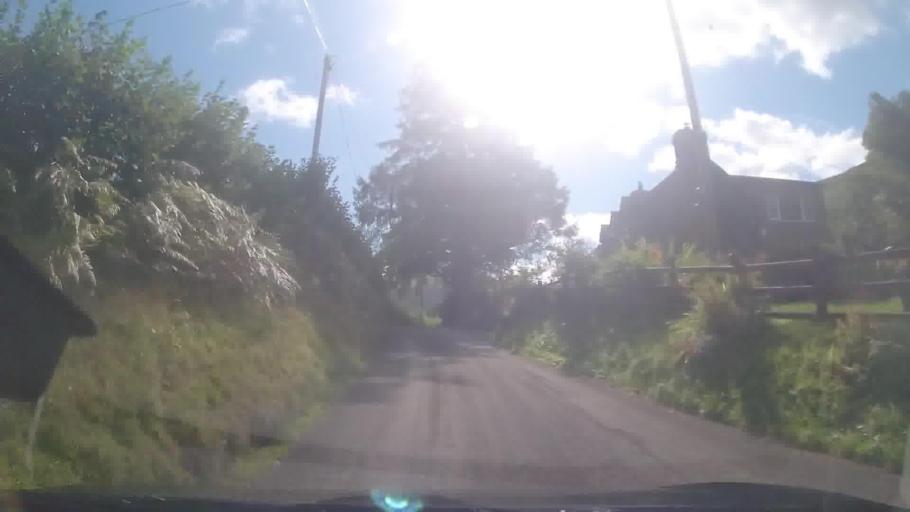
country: GB
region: Wales
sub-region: Gwynedd
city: Bala
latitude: 52.7682
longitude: -3.6251
